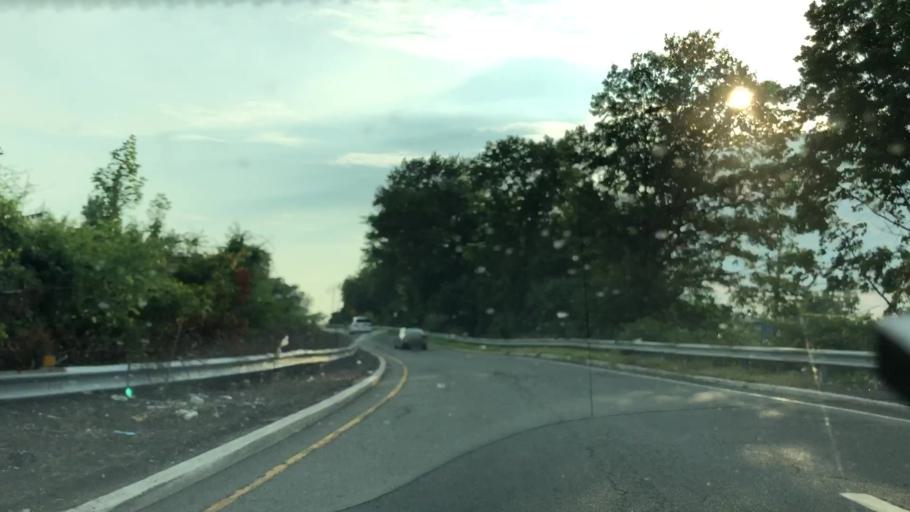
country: US
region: New Jersey
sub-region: Bergen County
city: Lyndhurst
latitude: 40.8264
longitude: -74.1256
